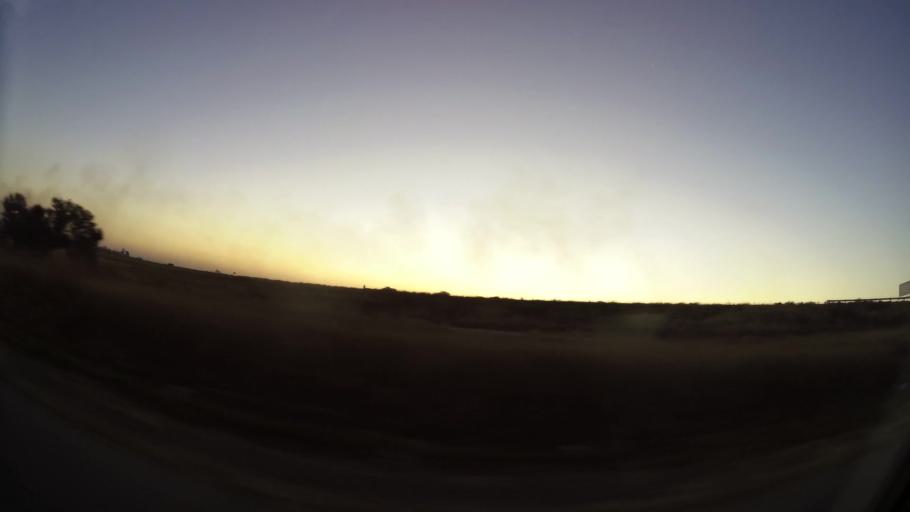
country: ZA
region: Gauteng
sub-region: City of Johannesburg Metropolitan Municipality
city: Diepsloot
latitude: -25.9150
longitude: 28.0257
